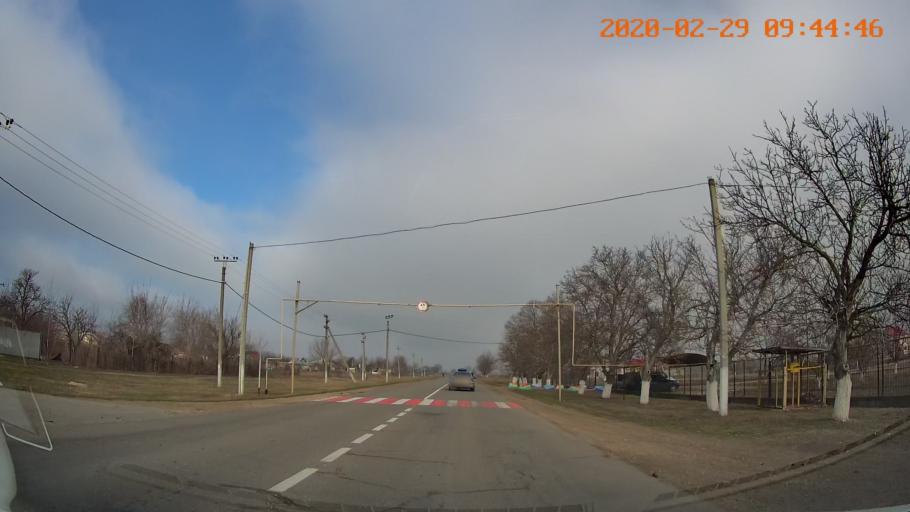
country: MD
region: Telenesti
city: Crasnoe
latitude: 46.6555
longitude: 29.8144
